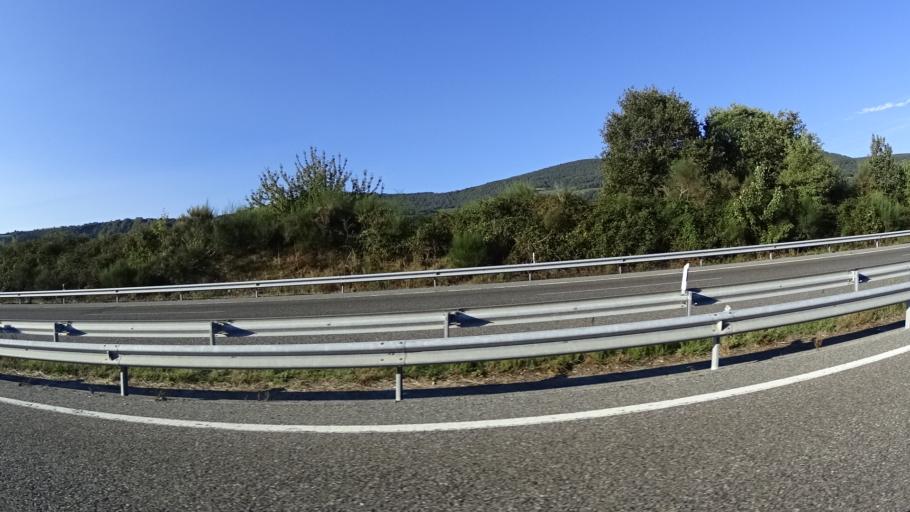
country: ES
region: Galicia
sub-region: Provincia de Lugo
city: San Roman
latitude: 42.7558
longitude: -7.0725
